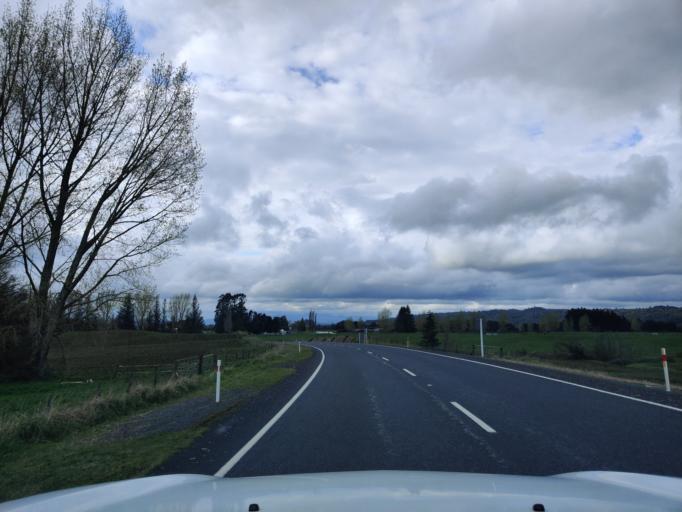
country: NZ
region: Waikato
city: Turangi
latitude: -39.0507
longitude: 175.3834
